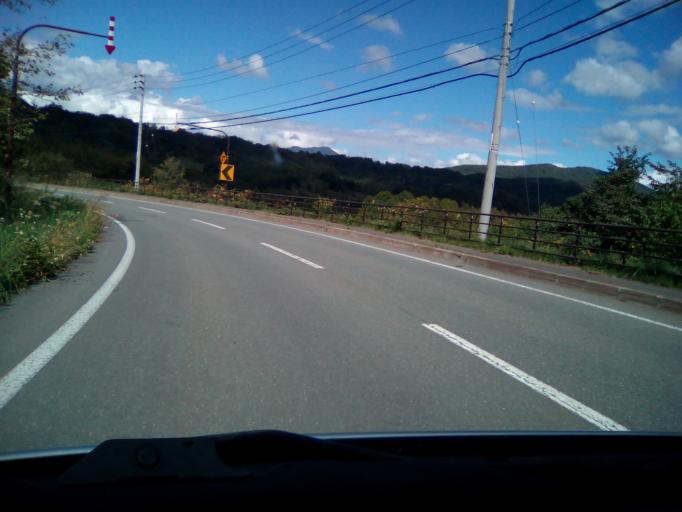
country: JP
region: Hokkaido
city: Date
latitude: 42.6462
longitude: 140.8155
